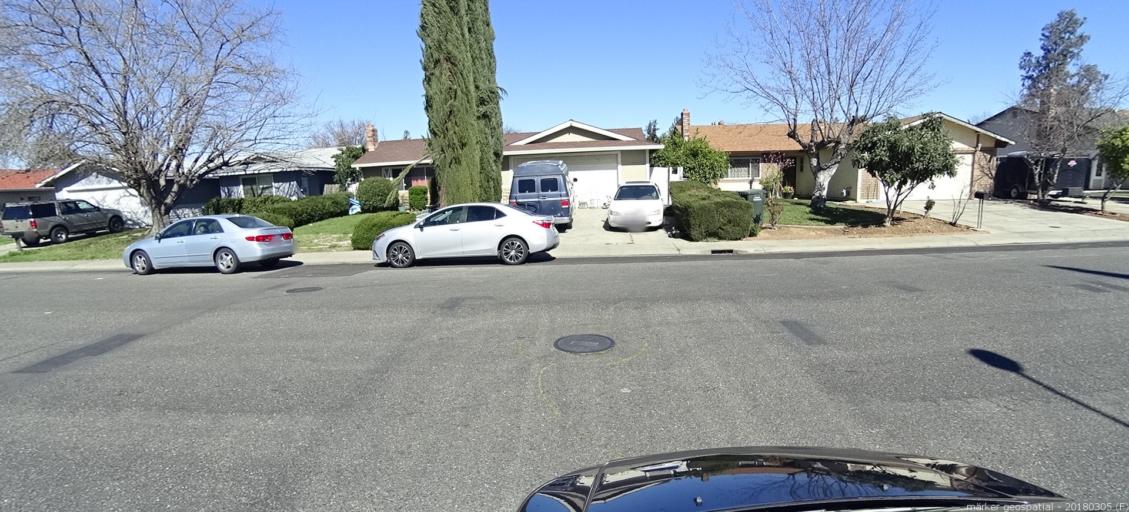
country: US
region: California
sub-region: Sacramento County
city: Florin
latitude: 38.4909
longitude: -121.3867
